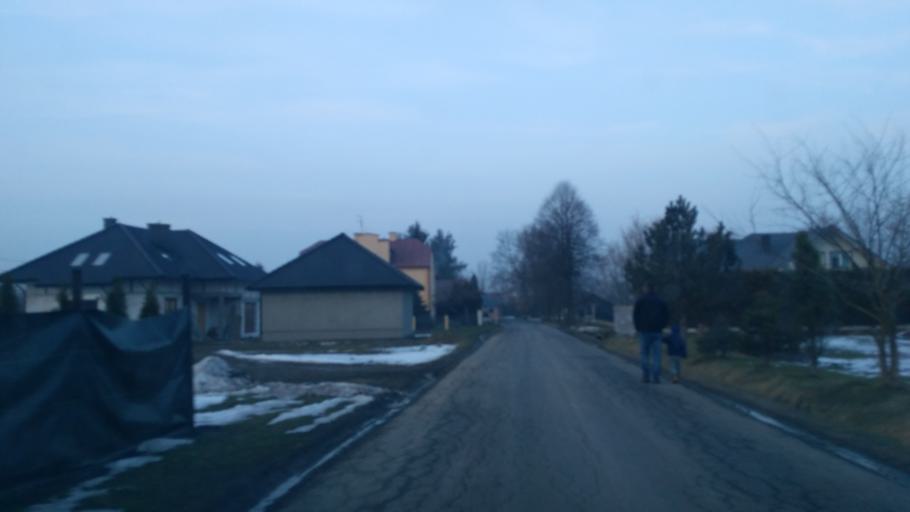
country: PL
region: Subcarpathian Voivodeship
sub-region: Powiat rzeszowski
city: Siedliska
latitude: 49.9630
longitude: 21.9719
